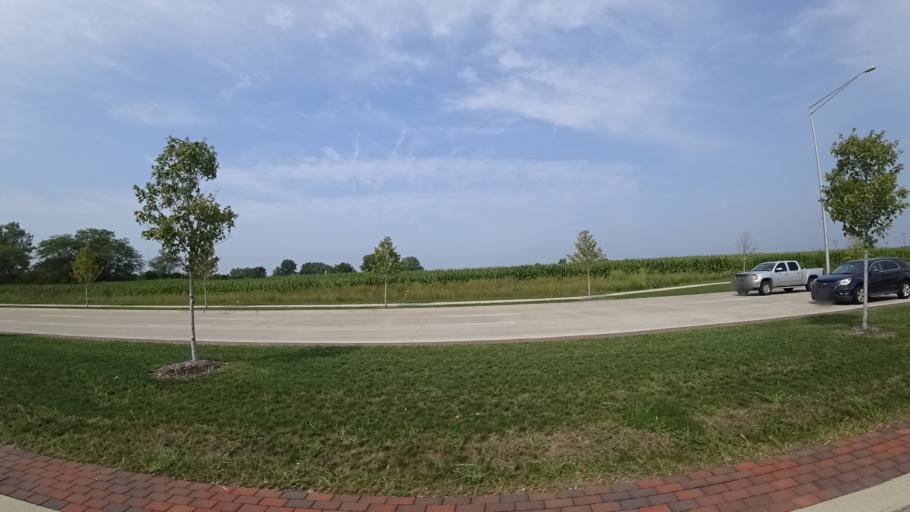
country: US
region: Illinois
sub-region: Cook County
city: Orland Hills
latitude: 41.5992
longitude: -87.8527
